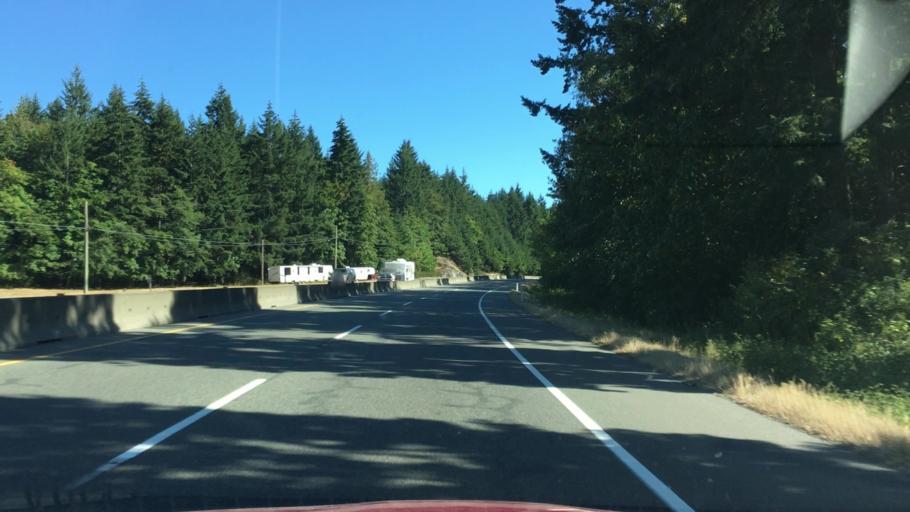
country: CA
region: British Columbia
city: North Cowichan
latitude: 48.8457
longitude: -123.7196
